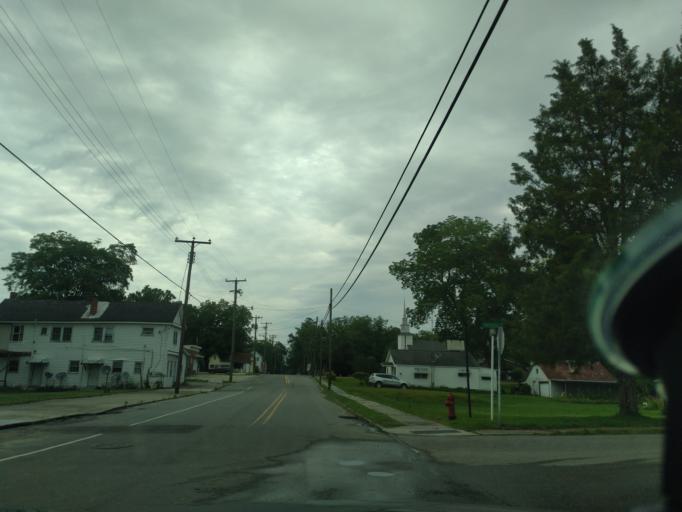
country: US
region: North Carolina
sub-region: Washington County
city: Plymouth
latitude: 35.8772
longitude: -76.6161
